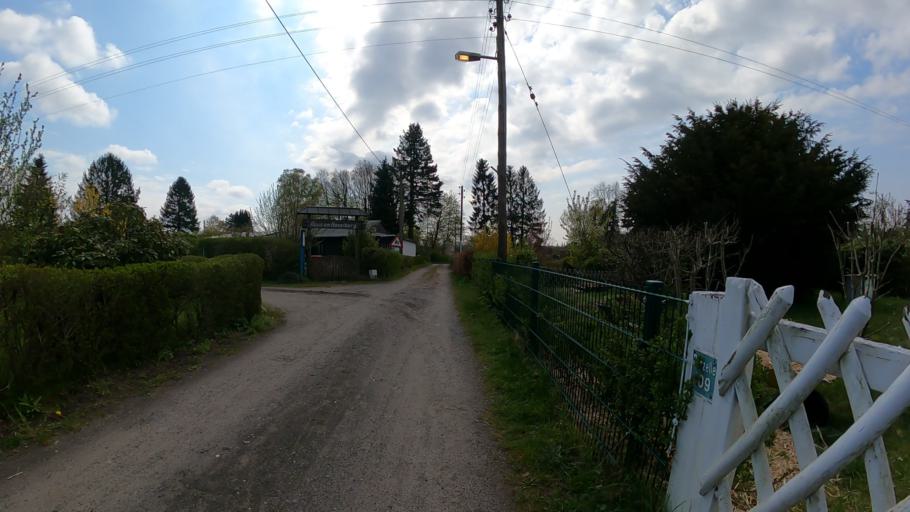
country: DE
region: Hamburg
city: Winterhude
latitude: 53.6179
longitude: 9.9933
